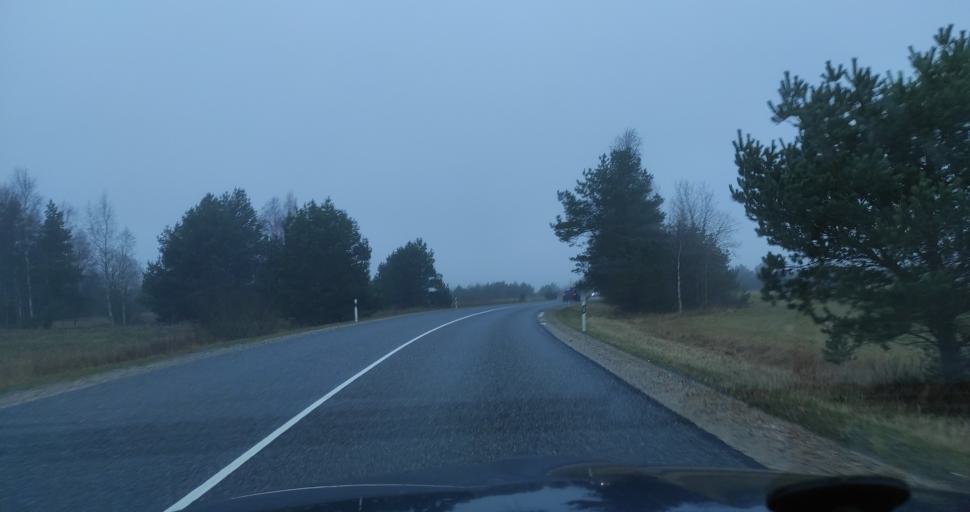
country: LV
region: Pavilostas
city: Pavilosta
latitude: 56.9650
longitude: 21.3379
